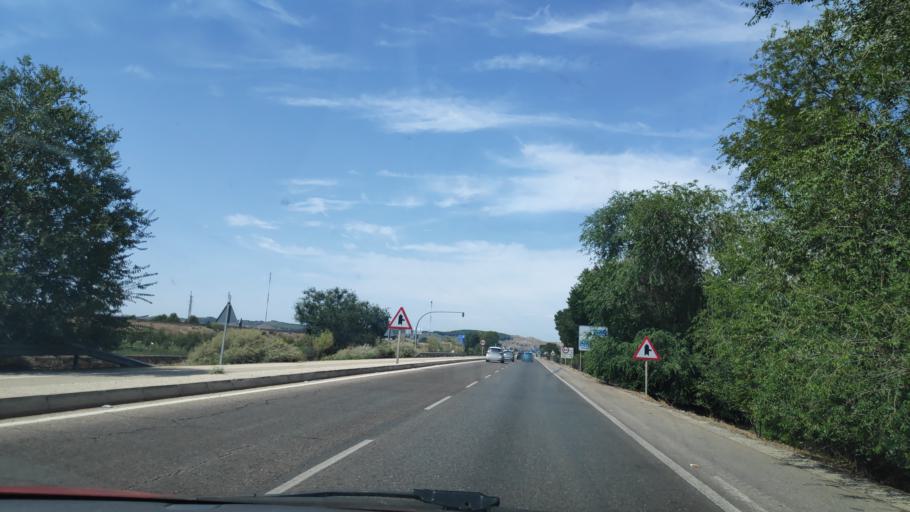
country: ES
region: Madrid
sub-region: Provincia de Madrid
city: Vaciamadrid
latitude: 40.3130
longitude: -3.4922
